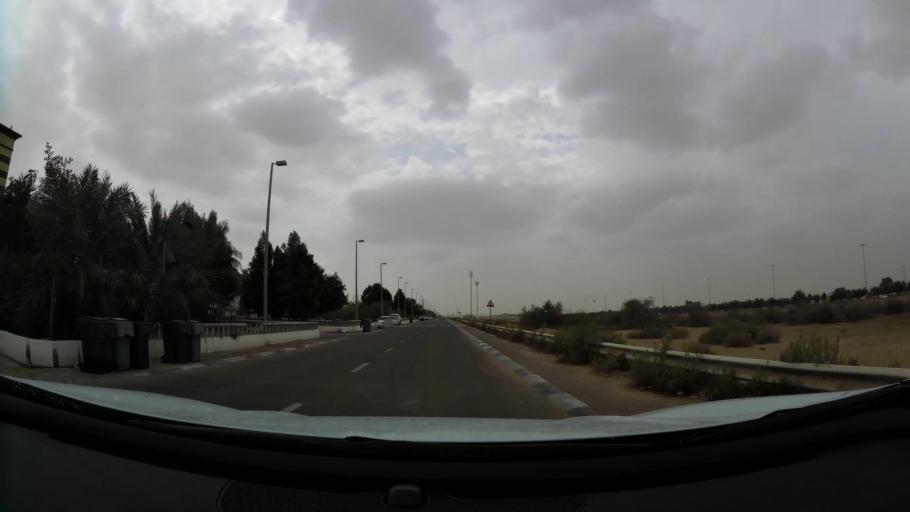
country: AE
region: Abu Dhabi
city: Abu Dhabi
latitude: 24.3592
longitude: 54.6518
